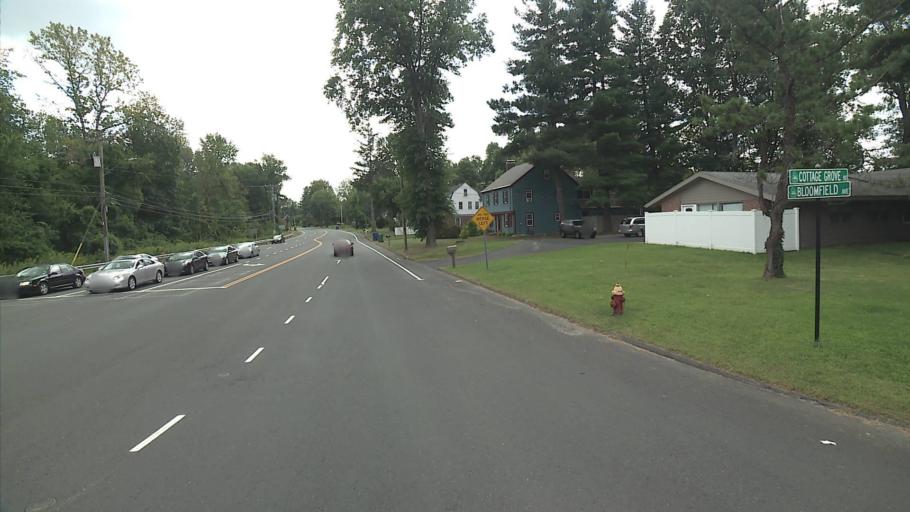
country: US
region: Connecticut
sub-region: Hartford County
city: Blue Hills
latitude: 41.8167
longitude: -72.7387
